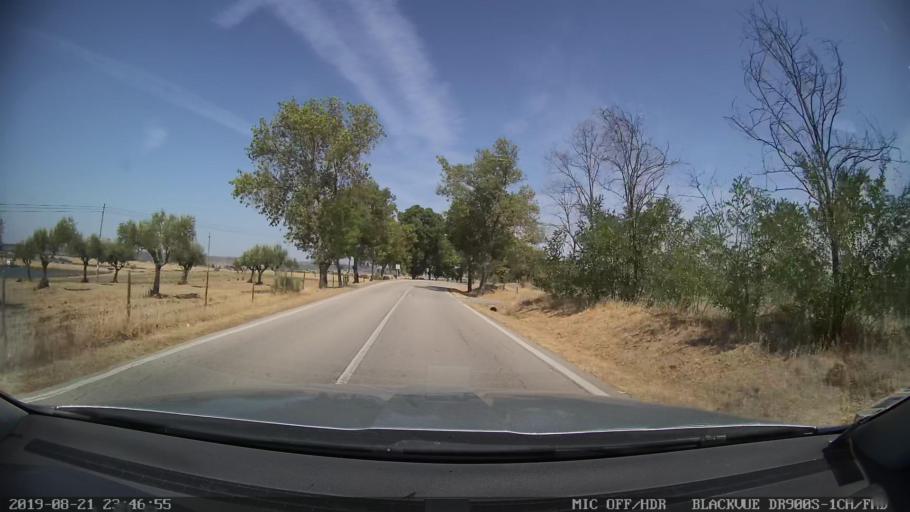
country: PT
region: Castelo Branco
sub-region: Idanha-A-Nova
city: Idanha-a-Nova
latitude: 39.8456
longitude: -7.2566
